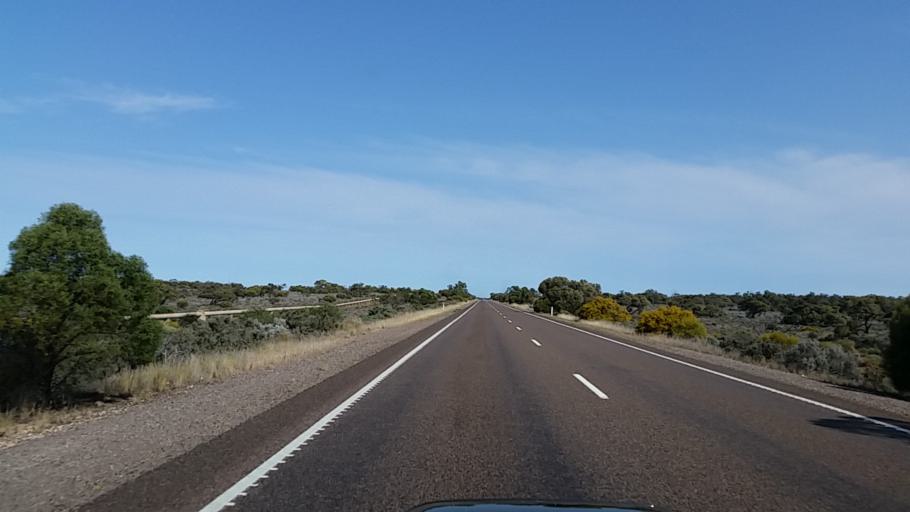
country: AU
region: South Australia
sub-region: Whyalla
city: Whyalla
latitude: -32.8208
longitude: 137.5440
